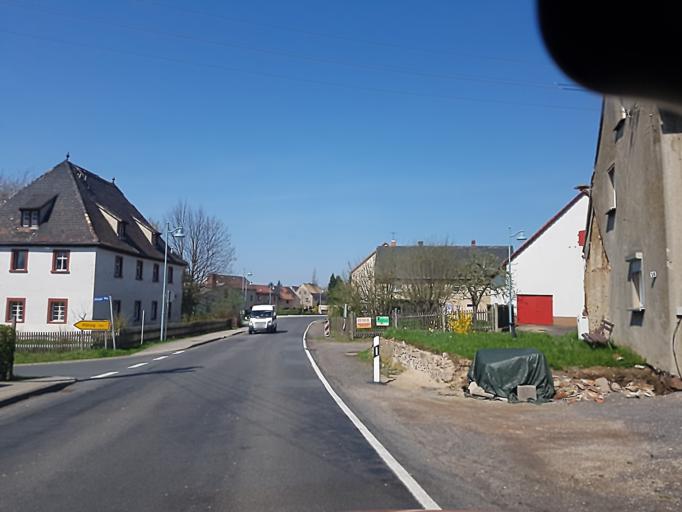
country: DE
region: Saxony
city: Ostrau
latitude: 51.2333
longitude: 12.8533
